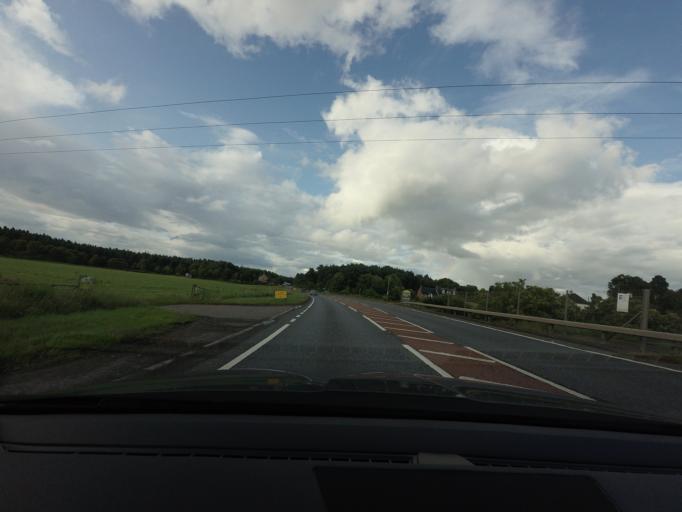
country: GB
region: Scotland
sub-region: Highland
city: Fortrose
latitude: 57.5224
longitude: -4.0639
